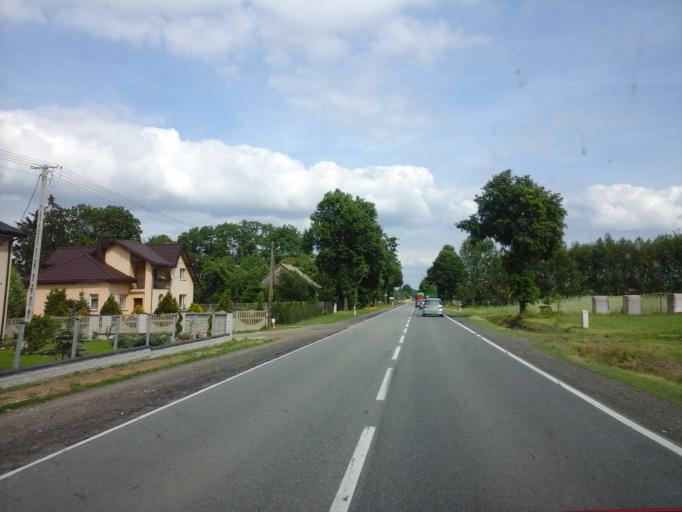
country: PL
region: Lodz Voivodeship
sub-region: Powiat opoczynski
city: Paradyz
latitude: 51.3083
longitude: 20.1006
